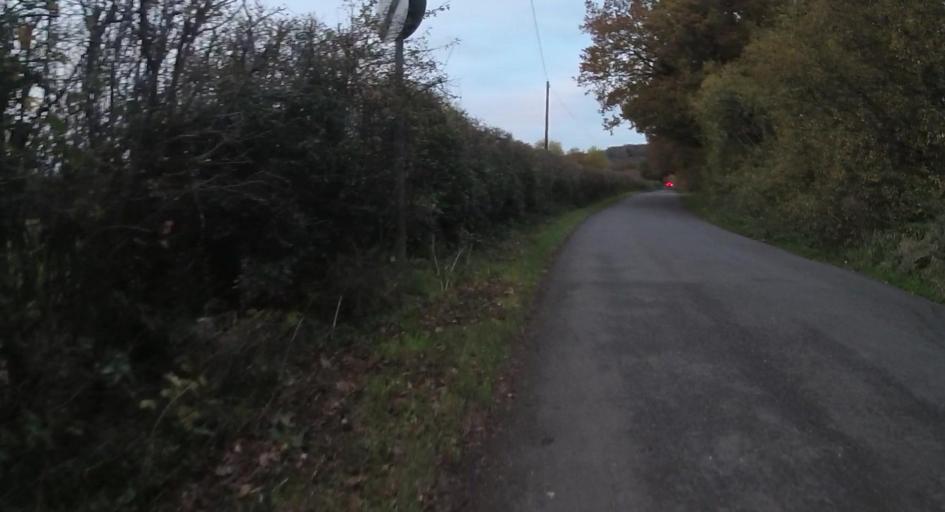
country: GB
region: England
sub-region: Hampshire
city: Kingsley
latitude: 51.1416
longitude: -0.8720
